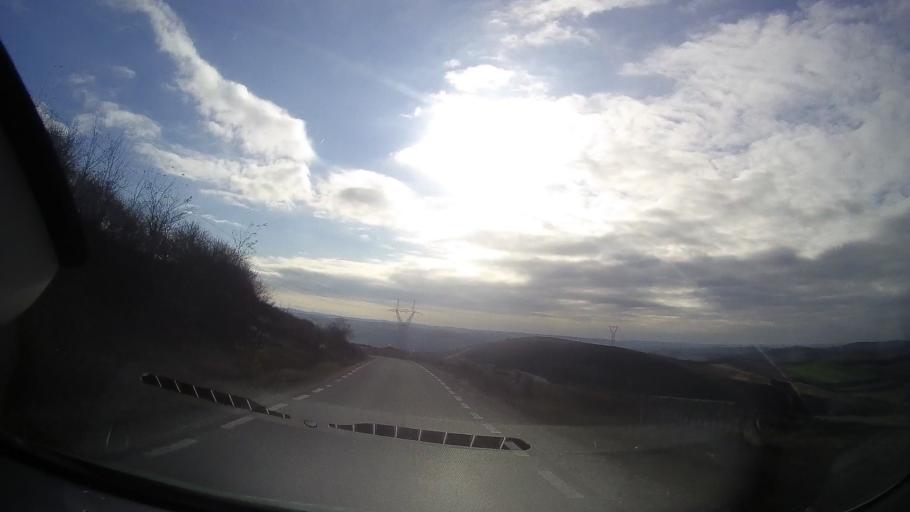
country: RO
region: Mures
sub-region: Comuna Sanger
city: Sanger
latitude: 46.5567
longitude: 24.1601
